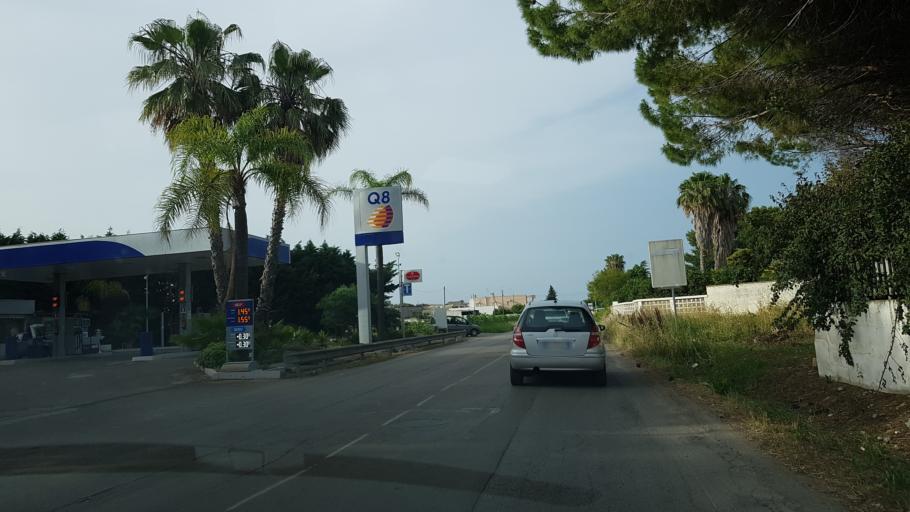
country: IT
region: Apulia
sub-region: Provincia di Brindisi
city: San Pietro Vernotico
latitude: 40.4932
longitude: 17.9900
